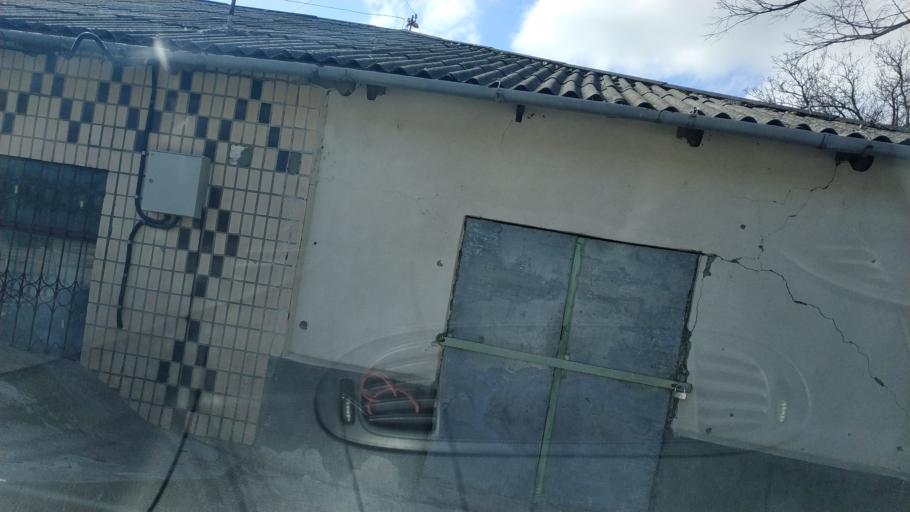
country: MD
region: Straseni
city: Straseni
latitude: 47.0181
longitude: 28.5446
